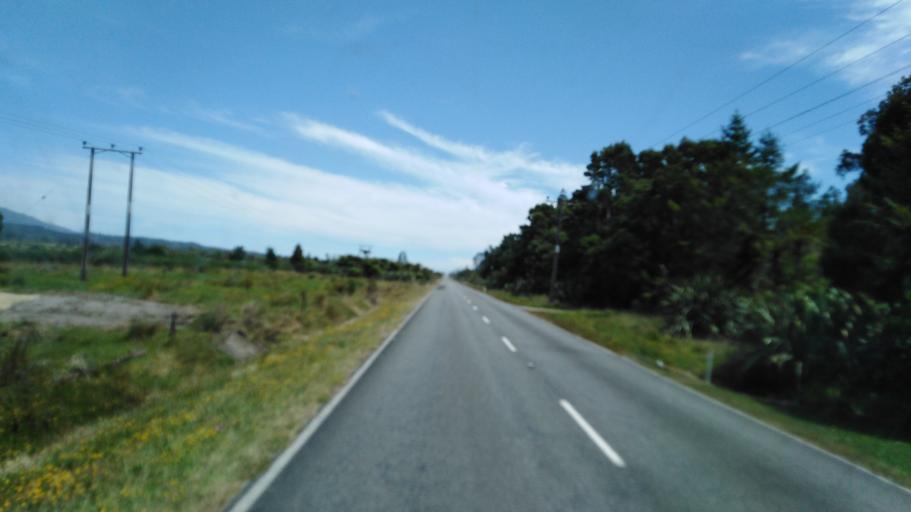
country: NZ
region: West Coast
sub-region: Buller District
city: Westport
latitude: -41.7407
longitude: 171.6970
